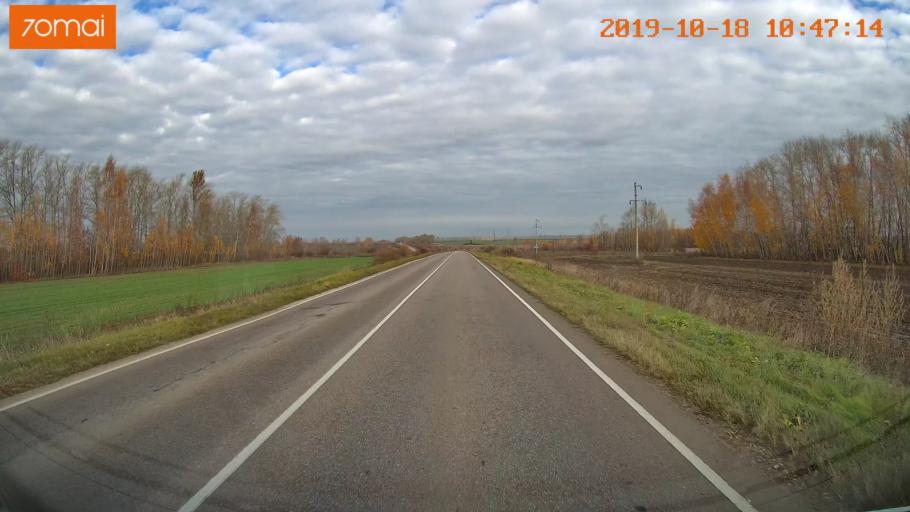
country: RU
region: Tula
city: Yepifan'
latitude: 53.6984
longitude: 38.6967
